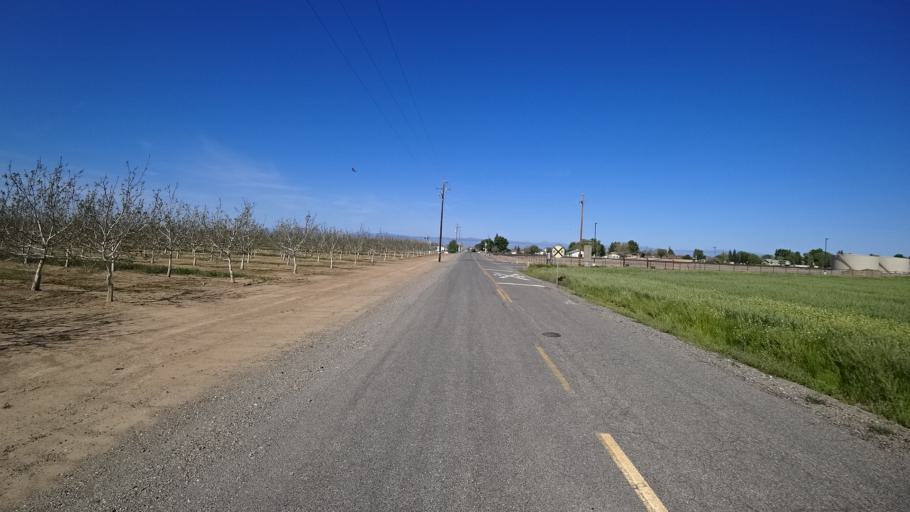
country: US
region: California
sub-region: Glenn County
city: Willows
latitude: 39.6113
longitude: -122.1919
